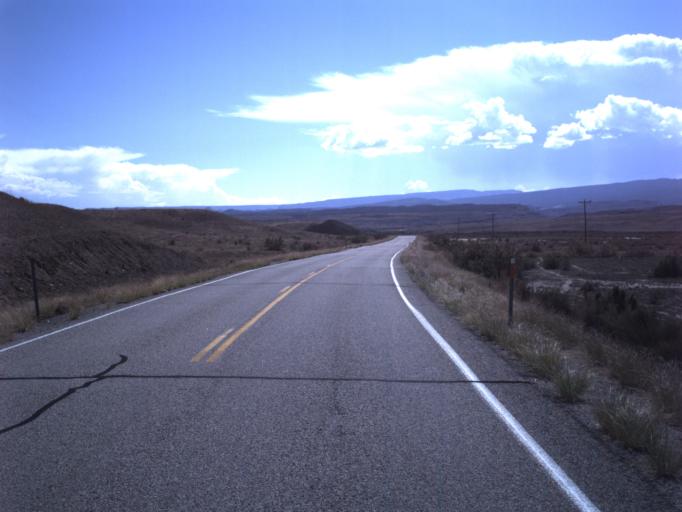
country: US
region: Utah
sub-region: Grand County
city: Moab
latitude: 38.8747
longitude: -109.3055
